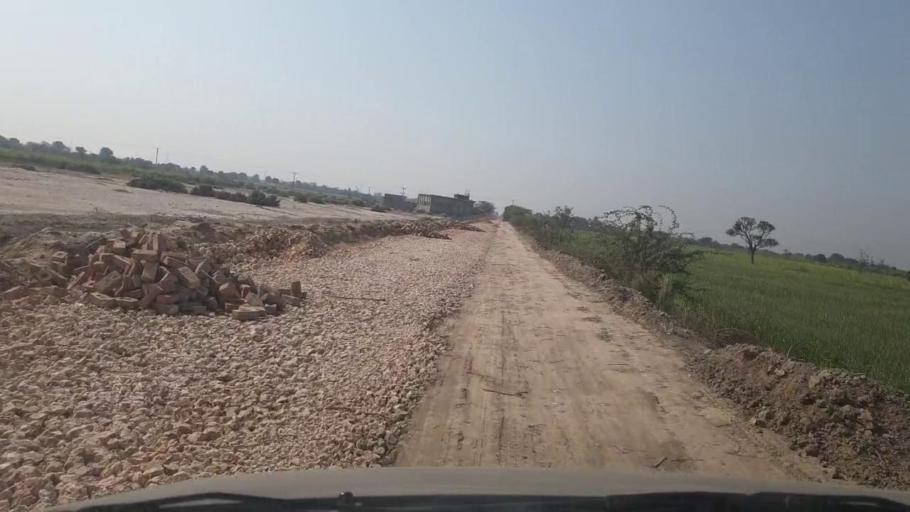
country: PK
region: Sindh
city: Mirwah Gorchani
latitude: 25.2575
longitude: 69.1140
